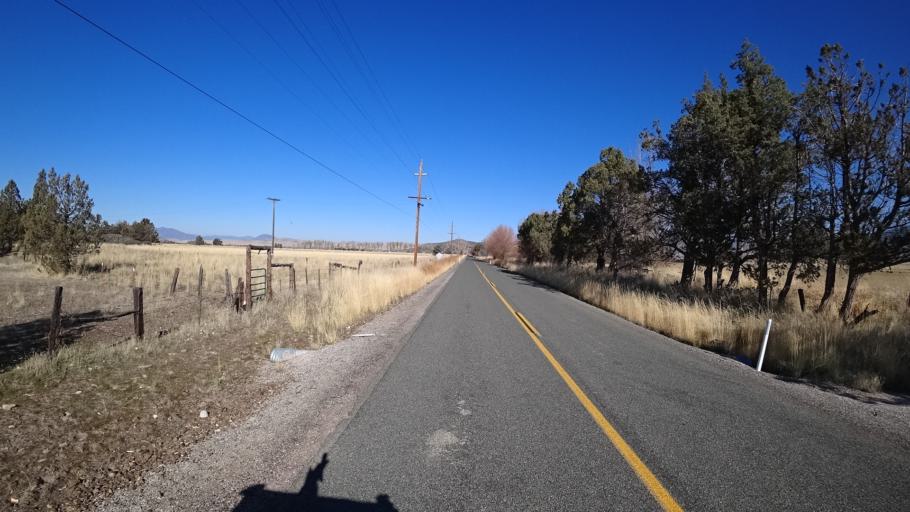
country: US
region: California
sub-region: Siskiyou County
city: Montague
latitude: 41.6744
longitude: -122.3699
